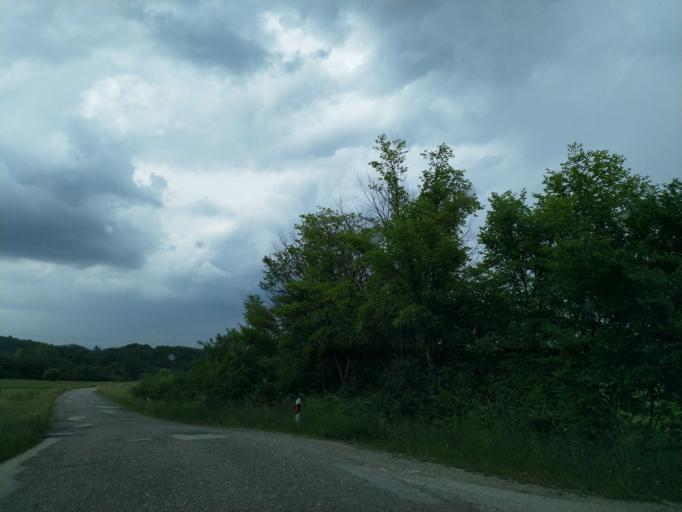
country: RS
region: Central Serbia
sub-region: Borski Okrug
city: Bor
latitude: 43.9849
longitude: 21.9739
